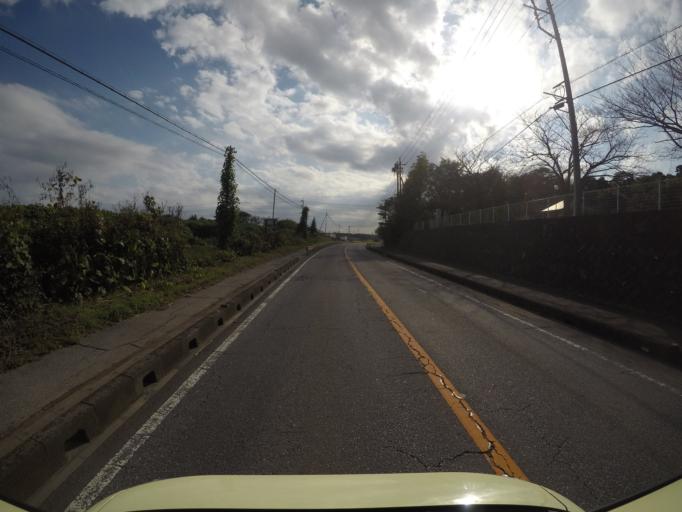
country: JP
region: Ibaraki
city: Iwai
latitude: 35.9950
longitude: 139.9028
